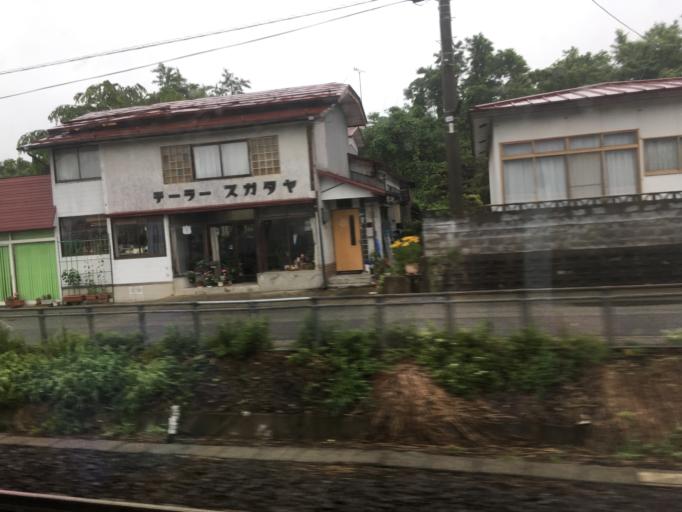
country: JP
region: Akita
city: Kakunodatemachi
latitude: 39.5903
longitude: 140.5703
